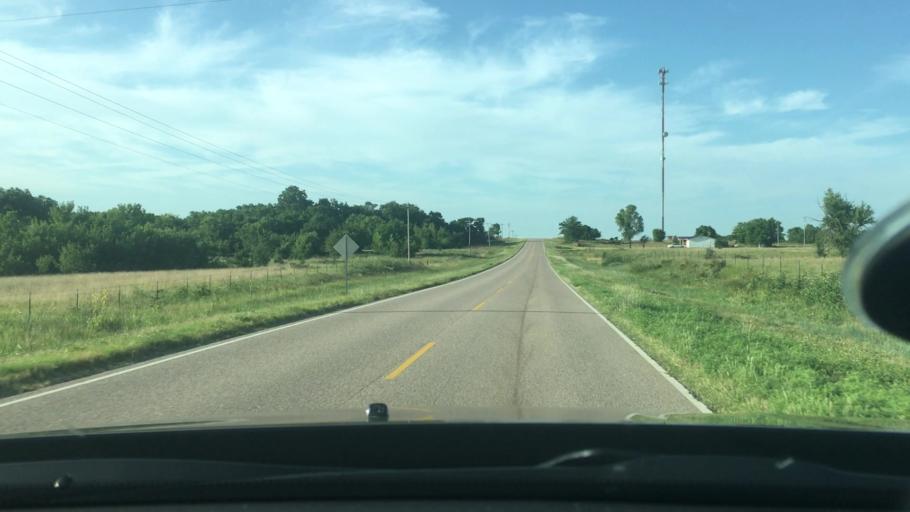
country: US
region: Oklahoma
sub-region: Johnston County
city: Tishomingo
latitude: 34.4365
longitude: -96.6378
